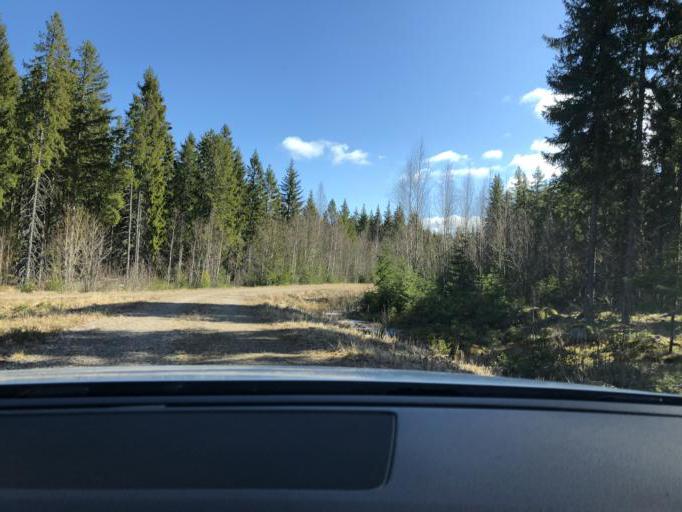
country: SE
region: Uppsala
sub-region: Heby Kommun
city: OEstervala
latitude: 60.2653
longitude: 17.1411
